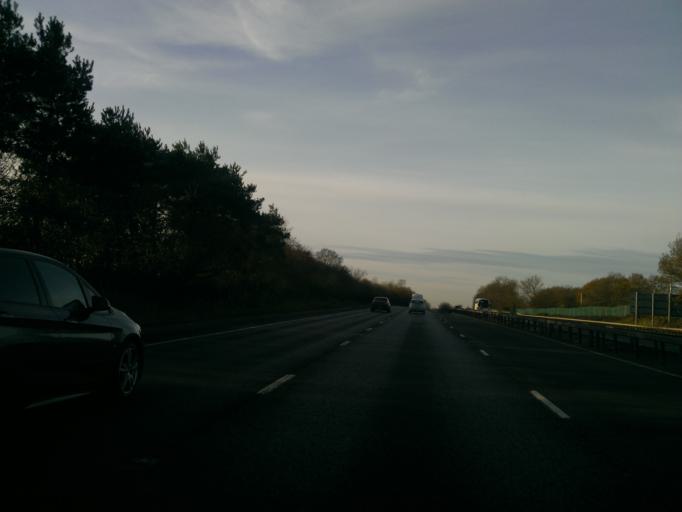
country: GB
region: England
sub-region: Essex
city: Hatfield Peverel
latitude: 51.7711
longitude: 0.5694
